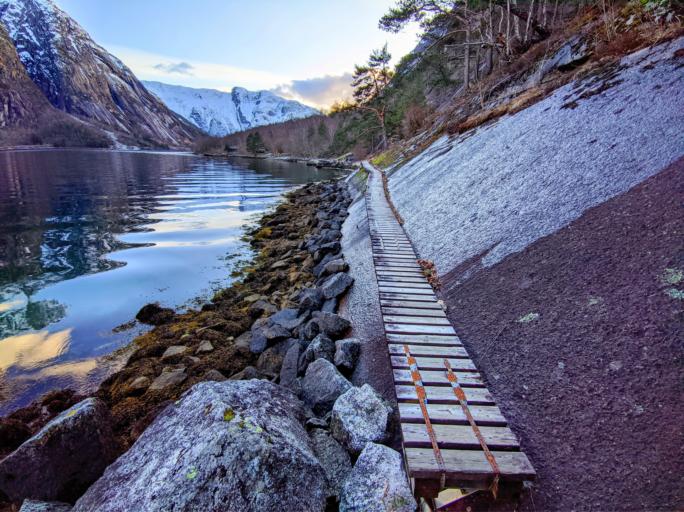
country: NO
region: Hordaland
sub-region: Eidfjord
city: Eidfjord
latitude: 60.4998
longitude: 7.1329
